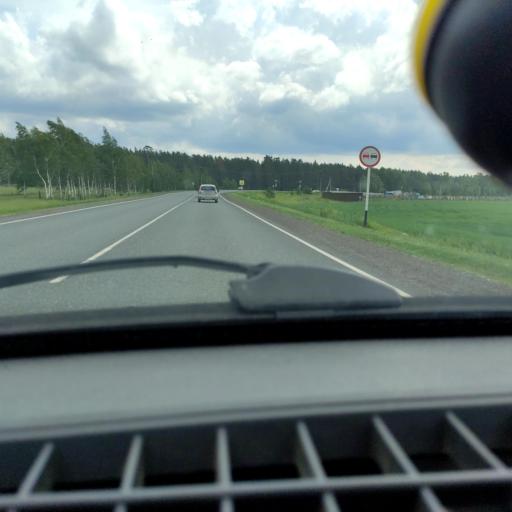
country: RU
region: Samara
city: Povolzhskiy
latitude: 53.6333
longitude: 49.6583
